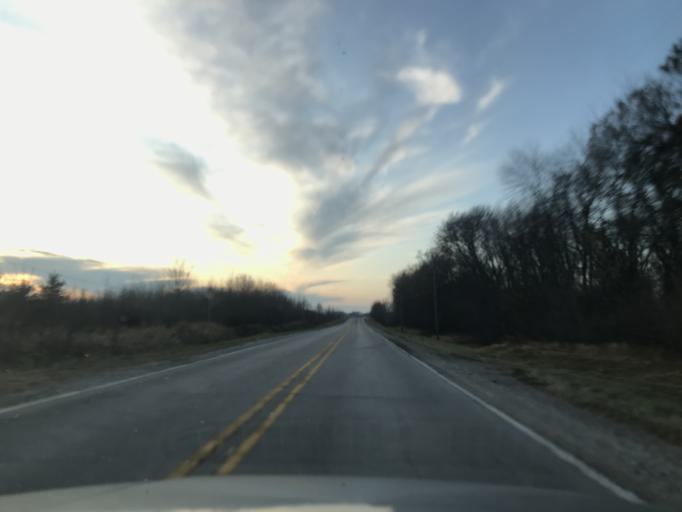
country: US
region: Illinois
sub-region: Henderson County
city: Oquawka
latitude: 41.0188
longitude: -90.8051
